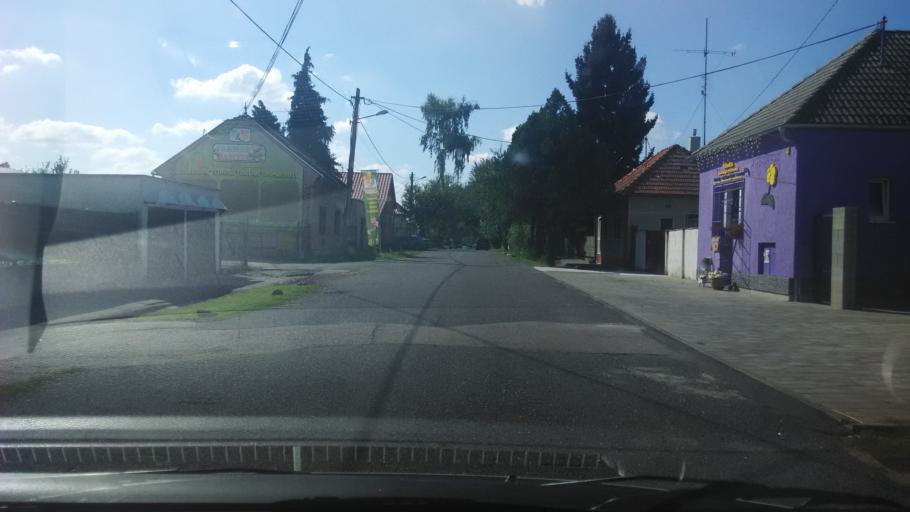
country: SK
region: Nitriansky
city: Levice
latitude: 48.2094
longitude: 18.6155
